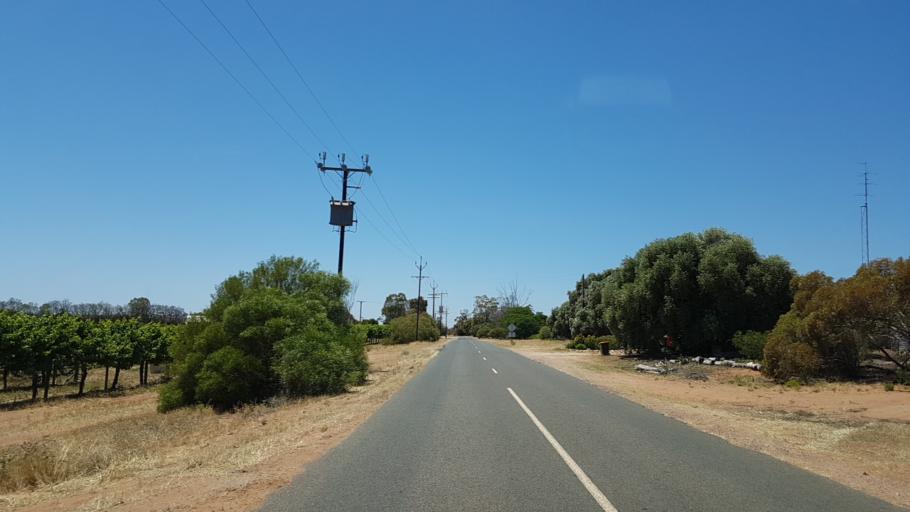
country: AU
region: South Australia
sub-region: Loxton Waikerie
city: Waikerie
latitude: -34.1698
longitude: 140.0337
